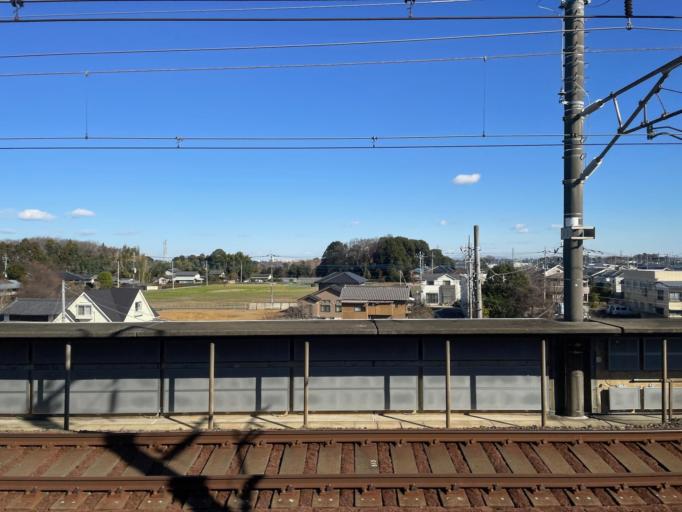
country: JP
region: Saitama
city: Ageoshimo
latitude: 36.0022
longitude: 139.6149
